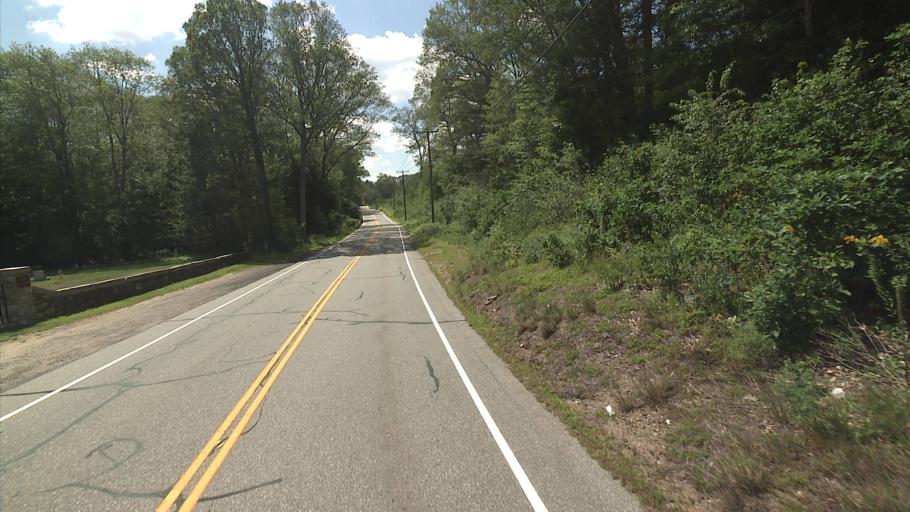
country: US
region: Connecticut
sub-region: Windham County
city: South Woodstock
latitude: 41.8926
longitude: -72.0795
